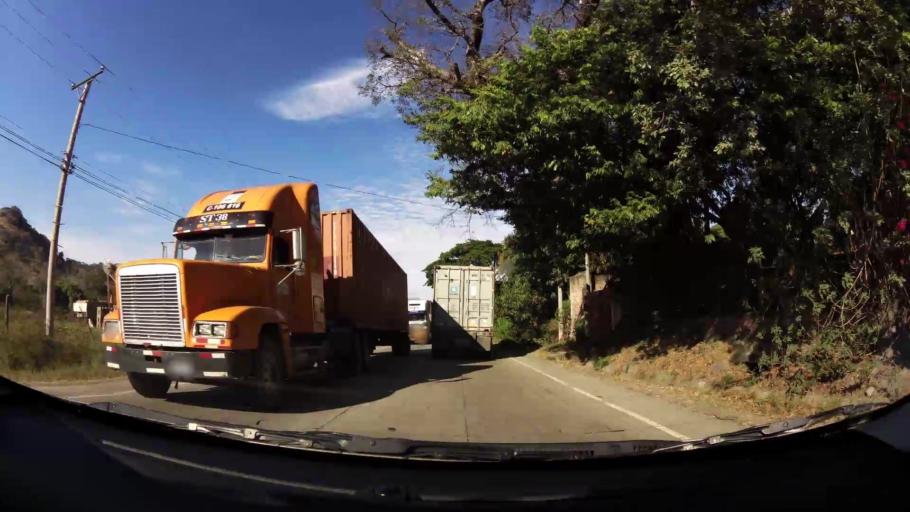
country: SV
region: Santa Ana
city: Texistepeque
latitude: 14.0781
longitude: -89.5012
